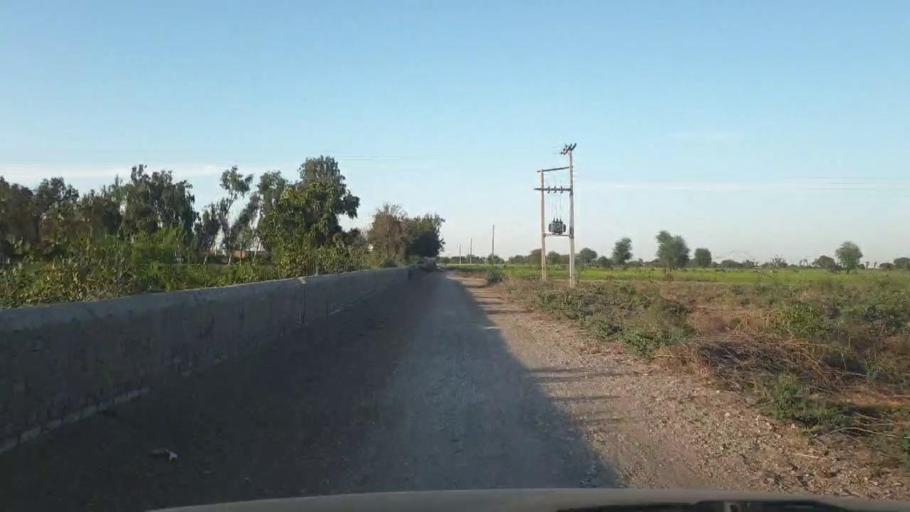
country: PK
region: Sindh
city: Dhoro Naro
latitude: 25.3961
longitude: 69.5755
